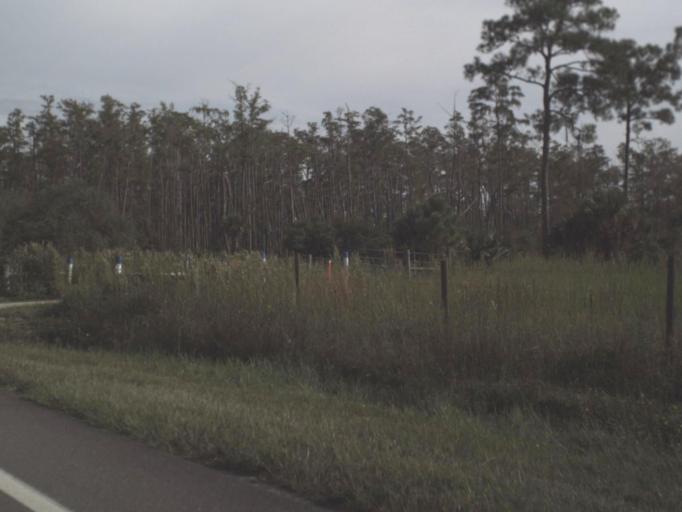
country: US
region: Florida
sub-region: Lee County
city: Olga
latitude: 26.9223
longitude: -81.7605
